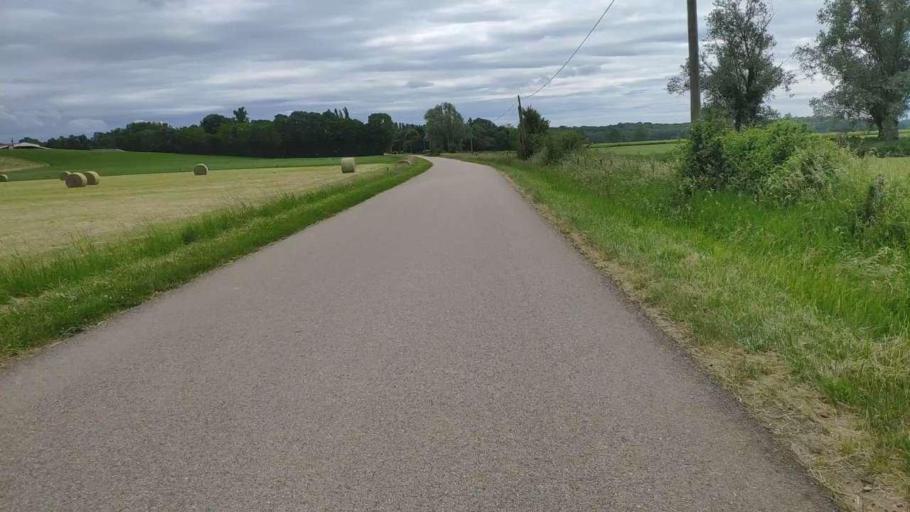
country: FR
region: Franche-Comte
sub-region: Departement du Jura
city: Bletterans
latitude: 46.7345
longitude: 5.4981
